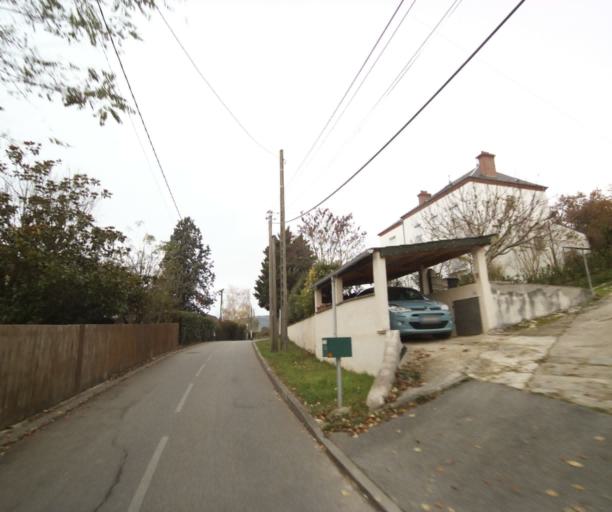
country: FR
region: Ile-de-France
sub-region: Departement des Yvelines
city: Triel-sur-Seine
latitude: 48.9898
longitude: 1.9978
